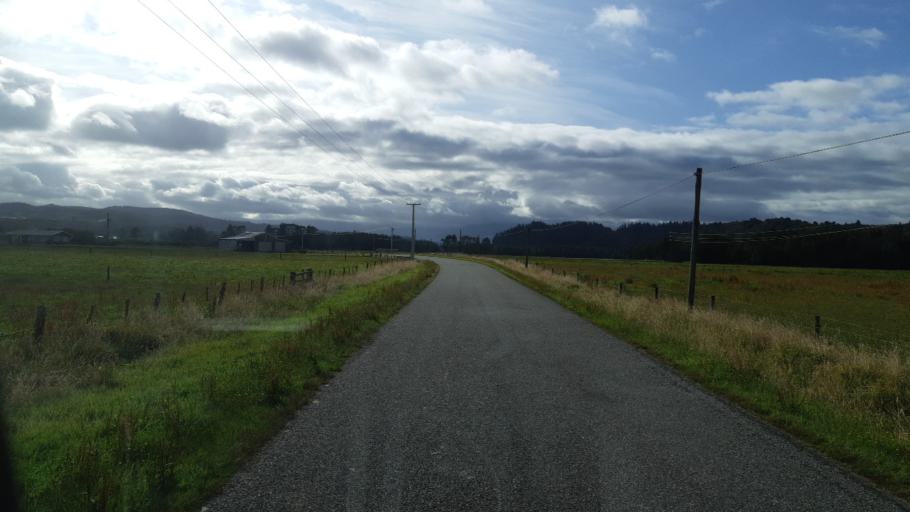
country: NZ
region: West Coast
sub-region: Westland District
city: Hokitika
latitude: -42.7341
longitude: 170.9692
